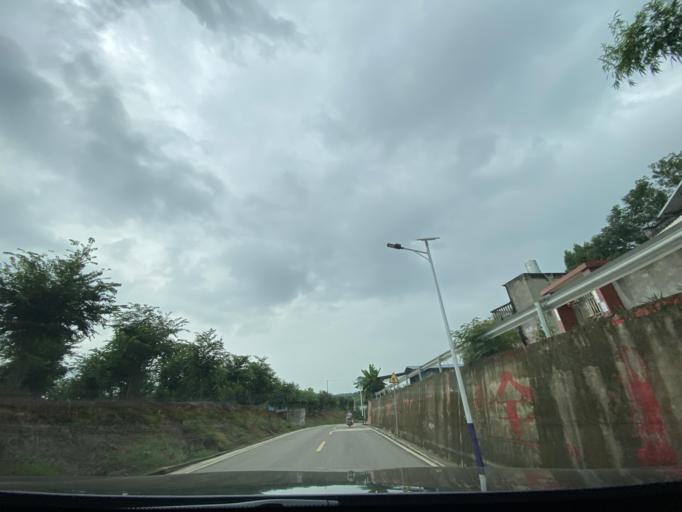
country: CN
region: Sichuan
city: Jiancheng
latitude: 30.5414
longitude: 104.5197
